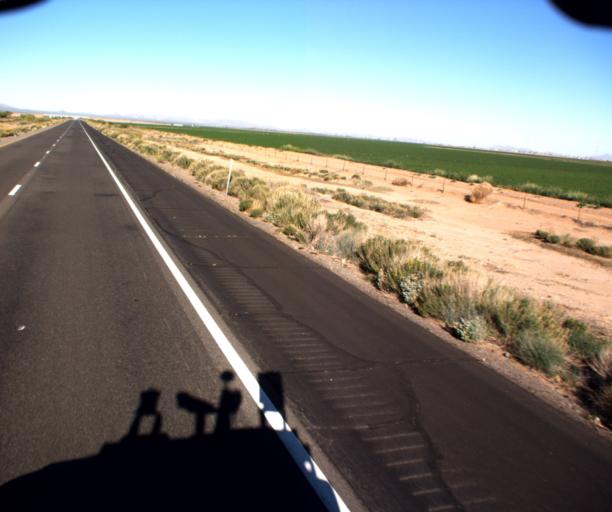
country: US
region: Arizona
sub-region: Pinal County
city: Casa Grande
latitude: 32.8283
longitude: -111.8979
